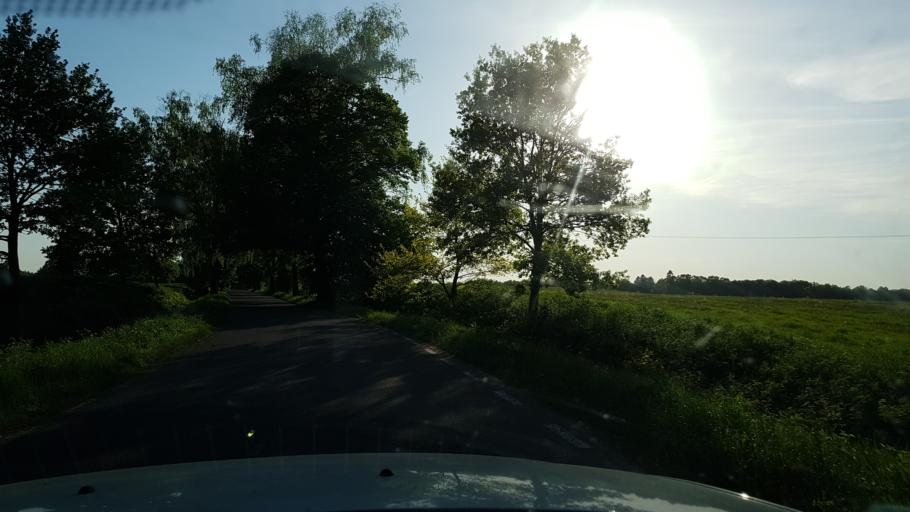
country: PL
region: West Pomeranian Voivodeship
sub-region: Powiat lobeski
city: Dobra
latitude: 53.5732
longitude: 15.2291
